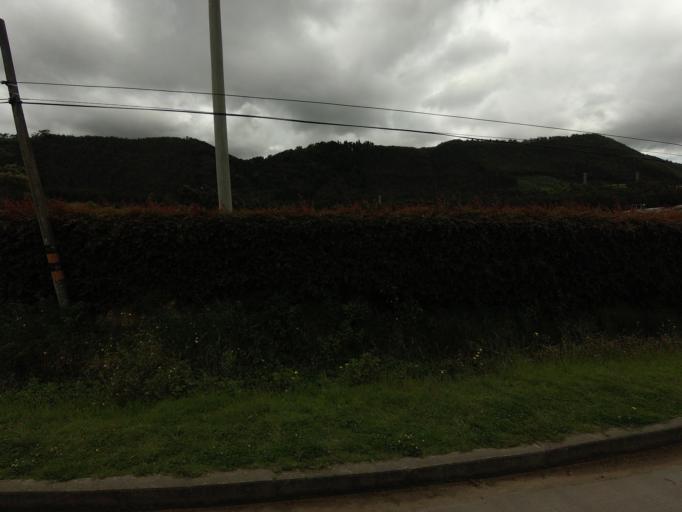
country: CO
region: Cundinamarca
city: Cajica
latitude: 4.9321
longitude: -74.0459
